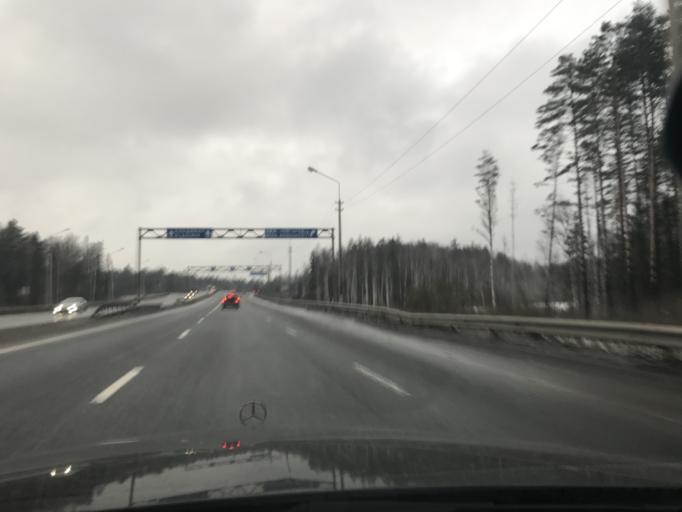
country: RU
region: Vladimir
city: Kameshkovo
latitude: 56.1902
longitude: 40.9504
